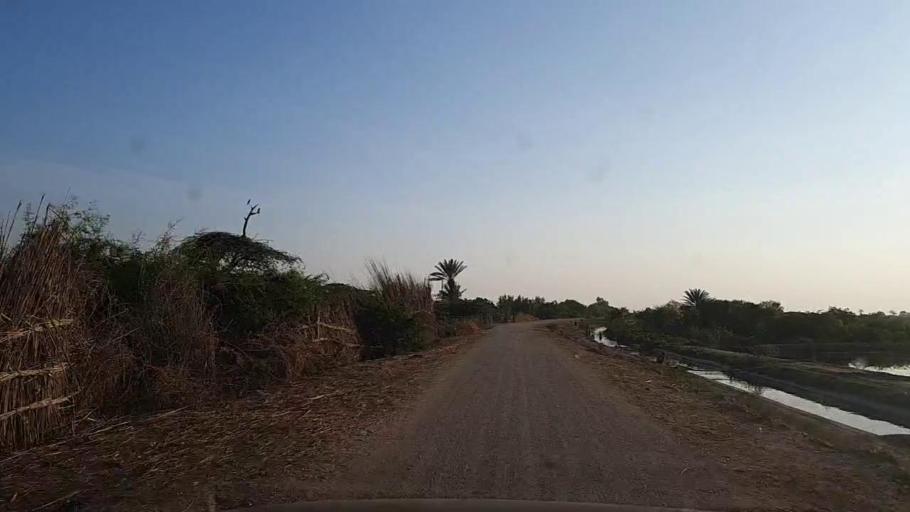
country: PK
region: Sindh
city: Thatta
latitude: 24.6220
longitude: 67.9138
